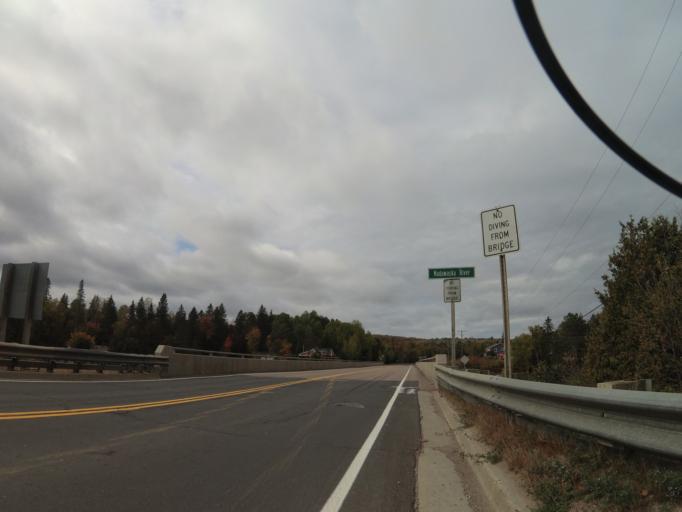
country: CA
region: Ontario
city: Renfrew
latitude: 45.2426
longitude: -77.1768
